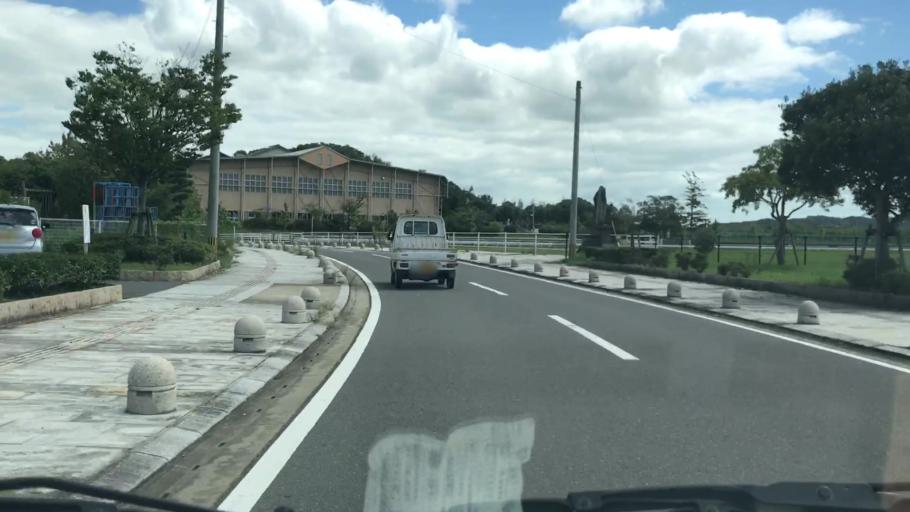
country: JP
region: Saga Prefecture
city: Takeocho-takeo
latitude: 33.2182
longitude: 130.0673
